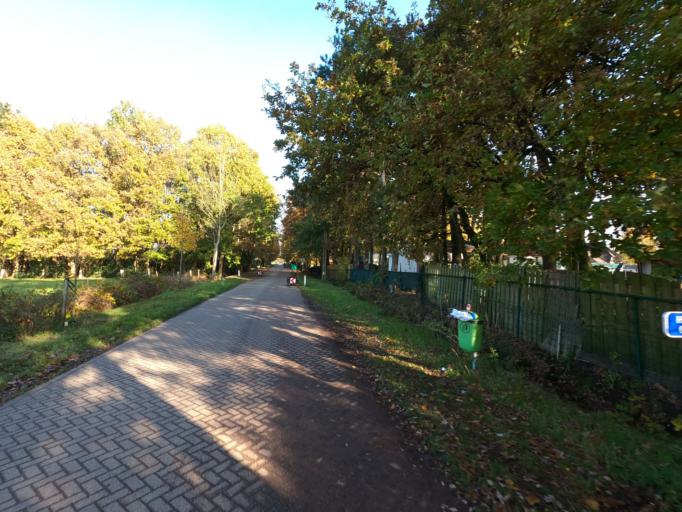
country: BE
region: Flanders
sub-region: Provincie Antwerpen
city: Wuustwezel
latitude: 51.3458
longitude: 4.5456
